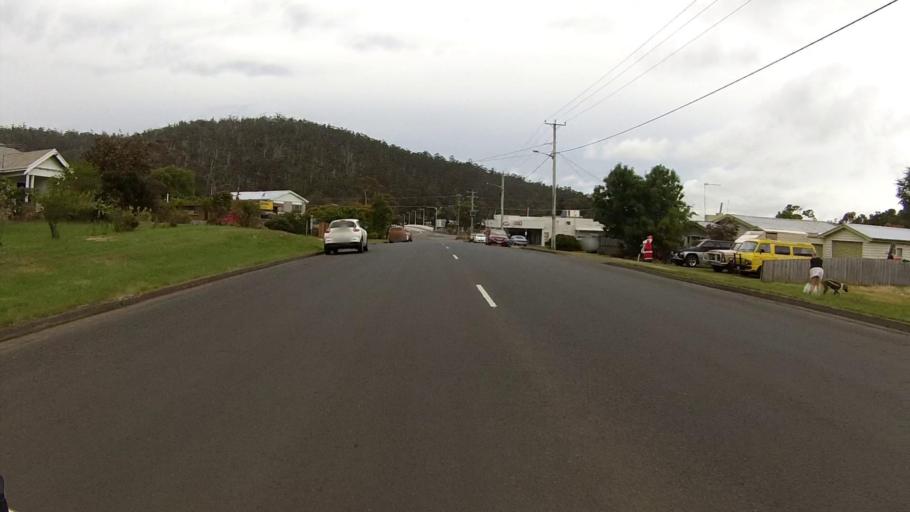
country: AU
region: Tasmania
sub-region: Sorell
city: Sorell
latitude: -42.5601
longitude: 147.8721
